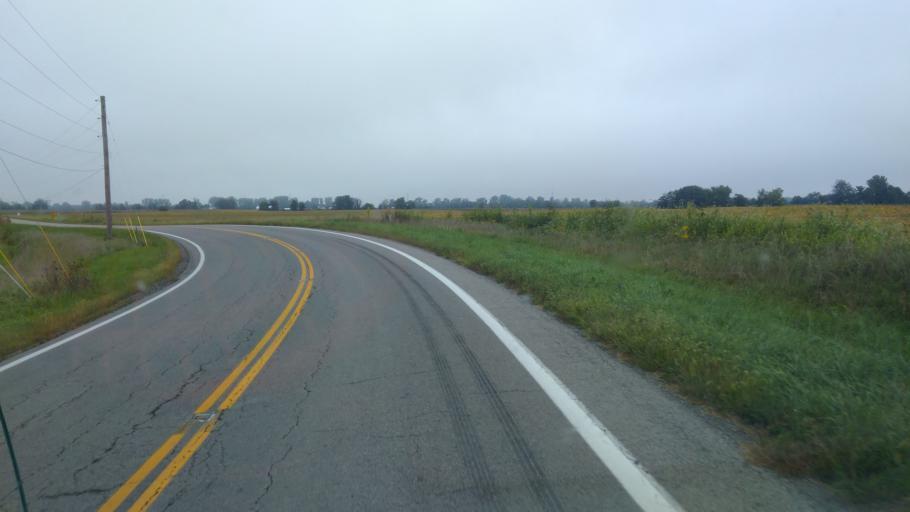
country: US
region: Ohio
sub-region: Logan County
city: Northwood
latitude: 40.4711
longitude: -83.5778
